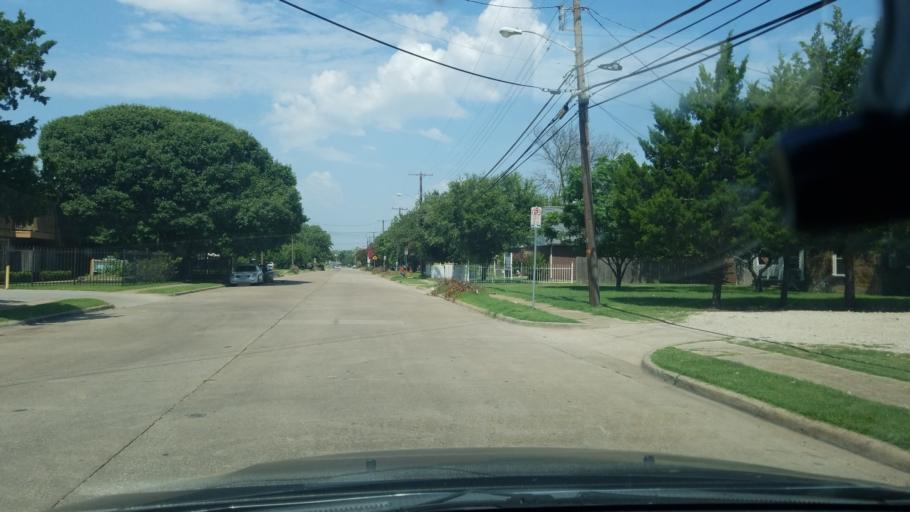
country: US
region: Texas
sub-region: Dallas County
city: Balch Springs
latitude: 32.7428
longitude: -96.6842
